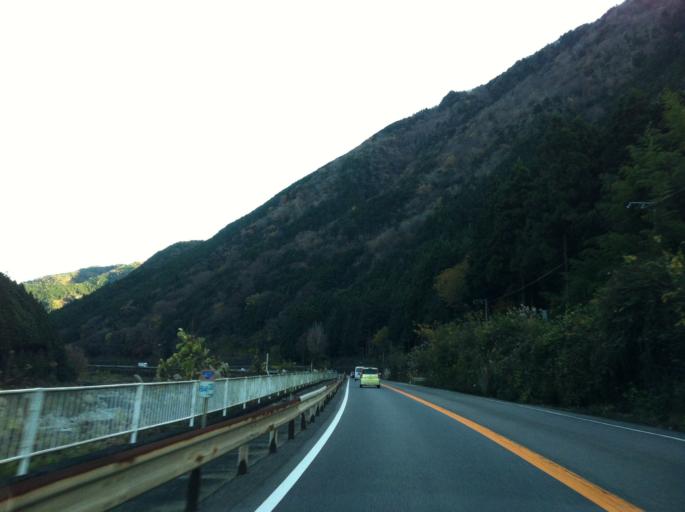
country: JP
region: Gifu
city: Mitake
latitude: 35.5852
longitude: 137.1724
